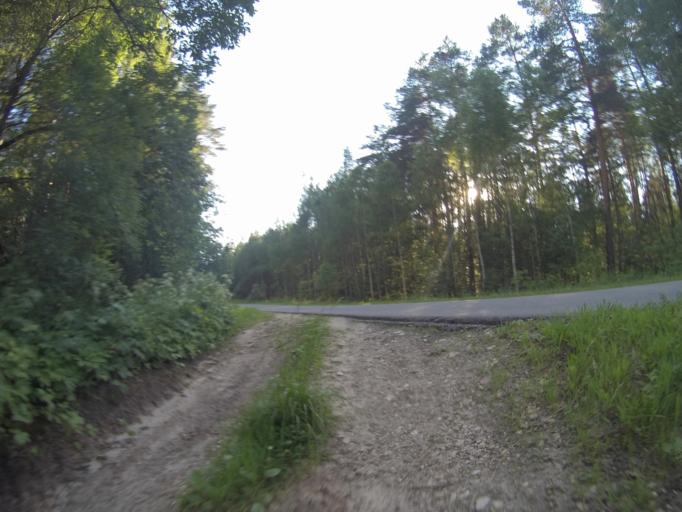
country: RU
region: Vladimir
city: Bogolyubovo
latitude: 56.1539
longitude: 40.5392
